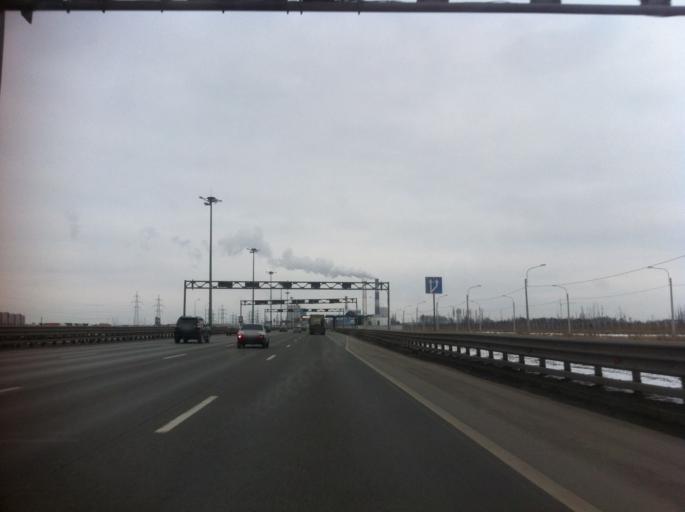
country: RU
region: St.-Petersburg
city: Shushary
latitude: 59.8200
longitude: 30.4117
